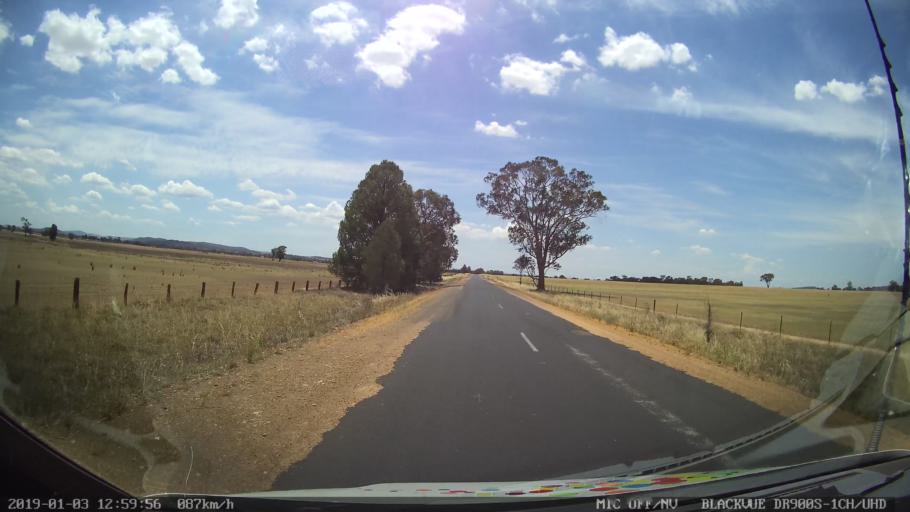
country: AU
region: New South Wales
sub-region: Cabonne
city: Canowindra
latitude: -33.6336
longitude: 148.3962
